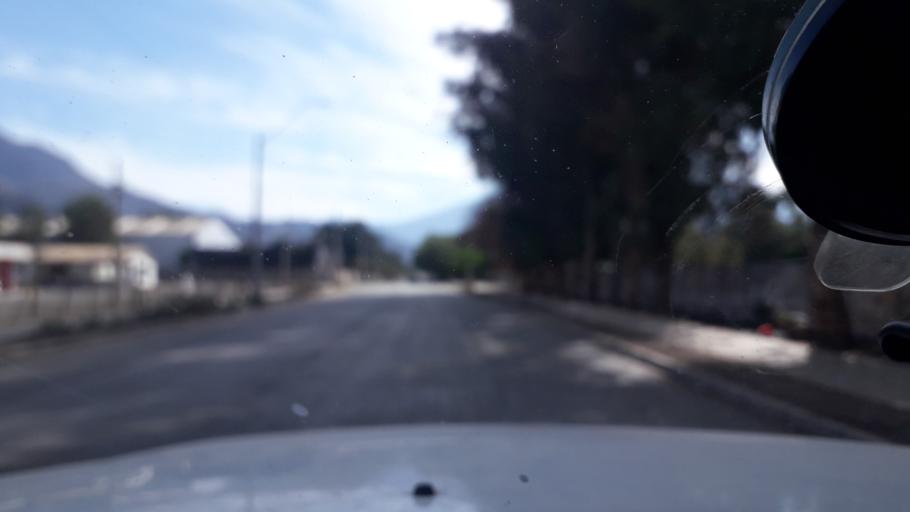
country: CL
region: Valparaiso
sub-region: Provincia de San Felipe
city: San Felipe
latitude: -32.7560
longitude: -70.7157
